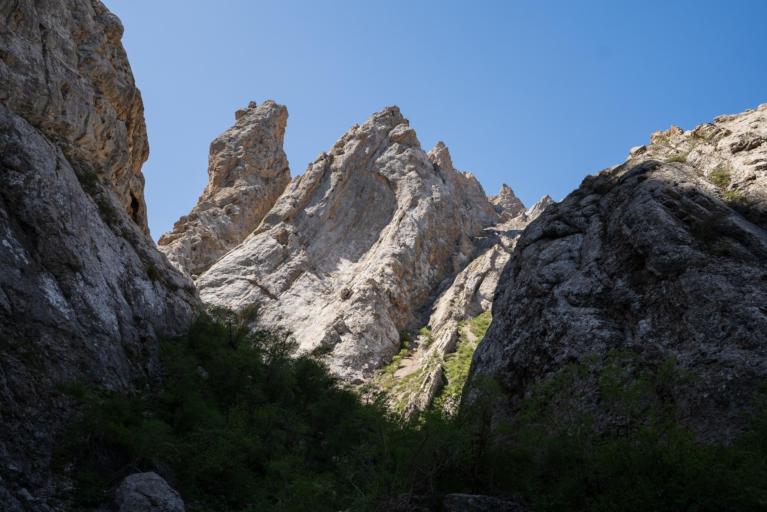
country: KZ
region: Ongtustik Qazaqstan
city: Ashchysay
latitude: 43.7707
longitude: 68.7962
